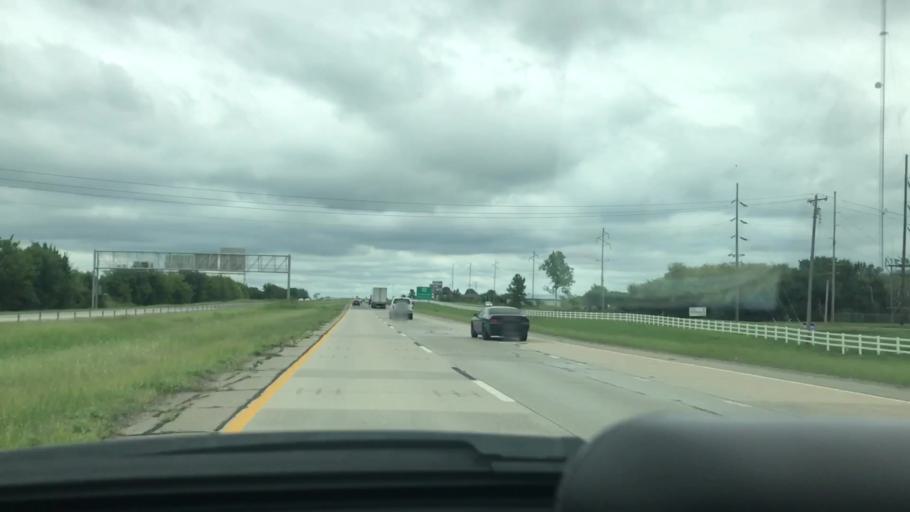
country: US
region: Oklahoma
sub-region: McIntosh County
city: Checotah
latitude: 35.4636
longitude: -95.5415
